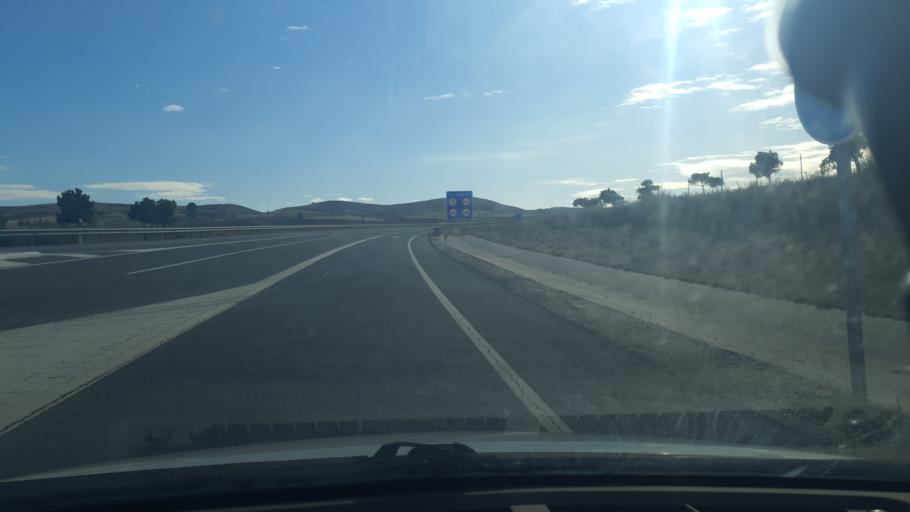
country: ES
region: Castille and Leon
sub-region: Provincia de Avila
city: Penalba de Avila
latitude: 40.7821
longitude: -4.7563
